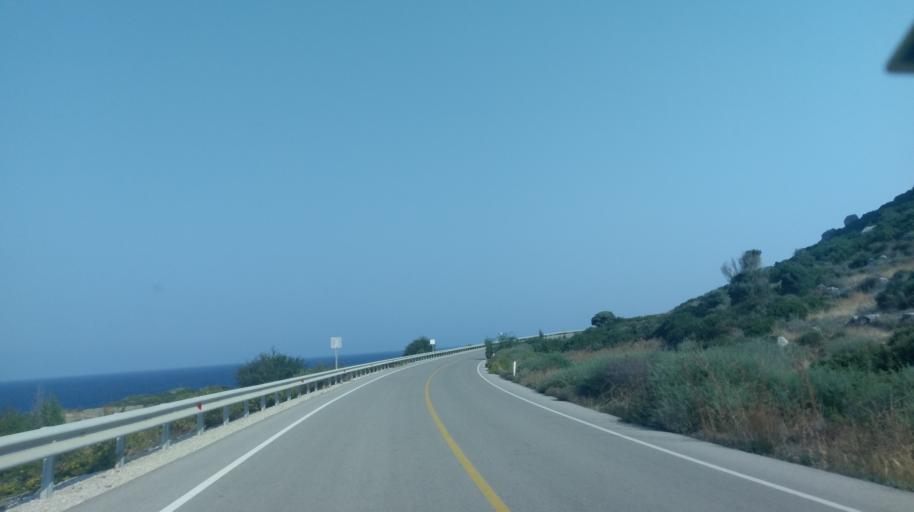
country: CY
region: Ammochostos
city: Leonarisso
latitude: 35.4692
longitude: 34.0351
